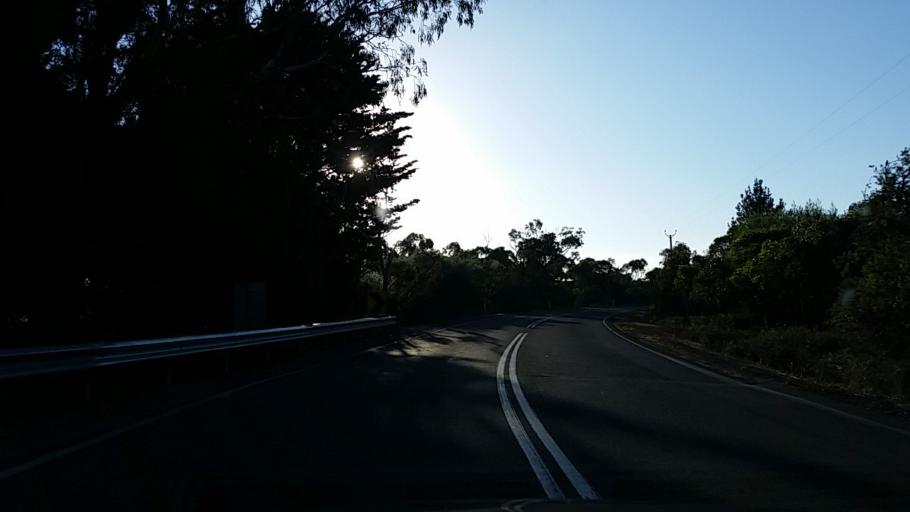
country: AU
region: South Australia
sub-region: Alexandrina
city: Mount Compass
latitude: -35.3688
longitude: 138.7328
